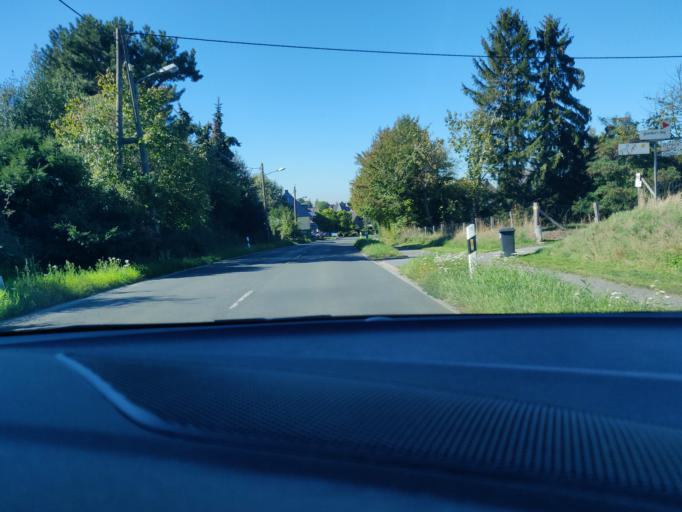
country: DE
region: North Rhine-Westphalia
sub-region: Regierungsbezirk Dusseldorf
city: Heiligenhaus
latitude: 51.3456
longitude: 6.9556
